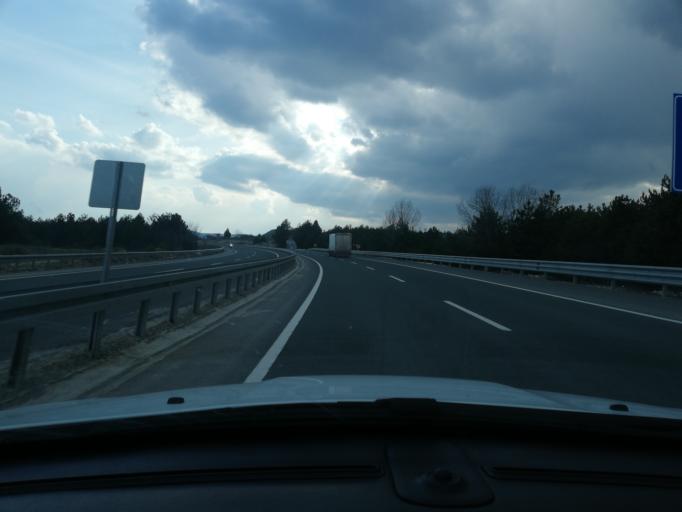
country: TR
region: Kastamonu
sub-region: Cide
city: Kastamonu
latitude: 41.3750
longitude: 33.7326
